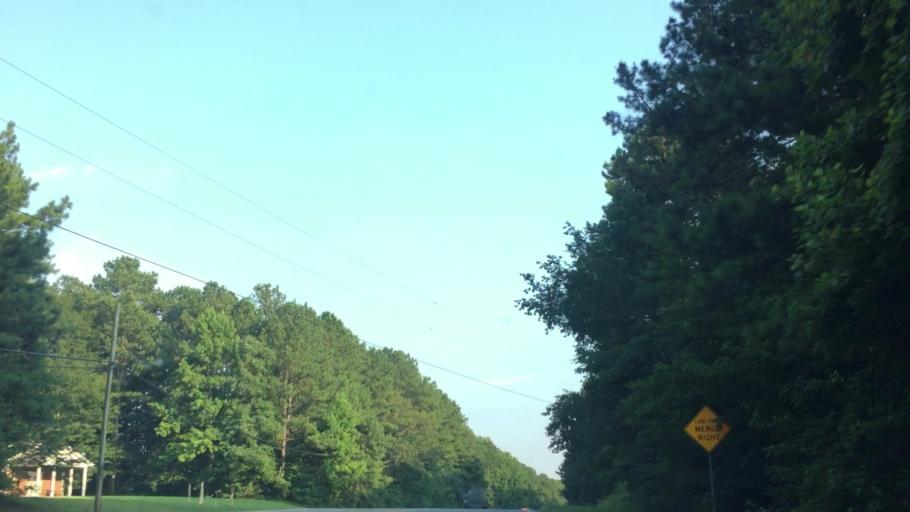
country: US
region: Georgia
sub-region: DeKalb County
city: Pine Mountain
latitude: 33.6430
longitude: -84.1861
